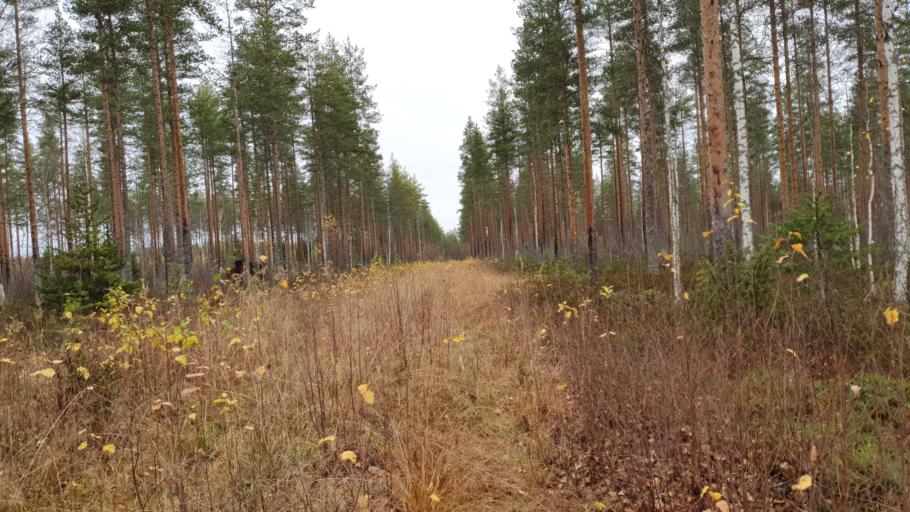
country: FI
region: Kainuu
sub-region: Kehys-Kainuu
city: Kuhmo
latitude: 64.1403
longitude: 29.4174
